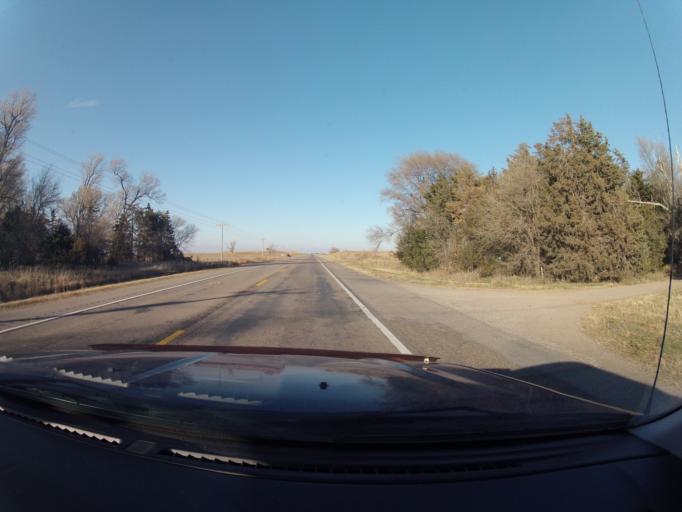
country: US
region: Nebraska
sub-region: Kearney County
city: Minden
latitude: 40.6115
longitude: -98.9515
